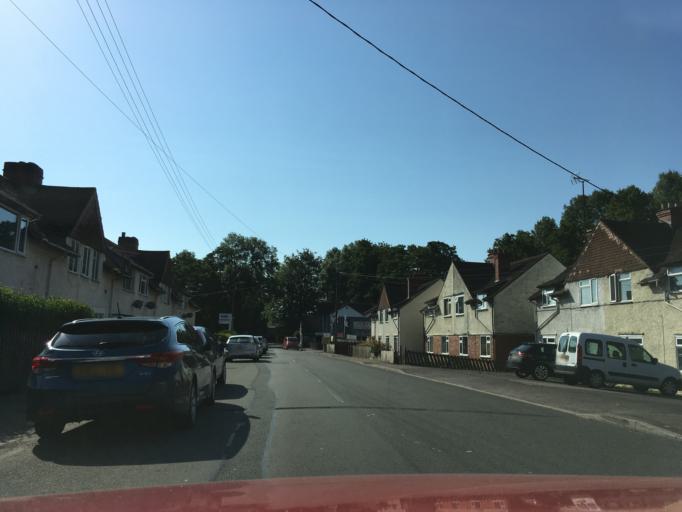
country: GB
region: England
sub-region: Gloucestershire
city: Lydney
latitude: 51.7289
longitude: -2.5339
